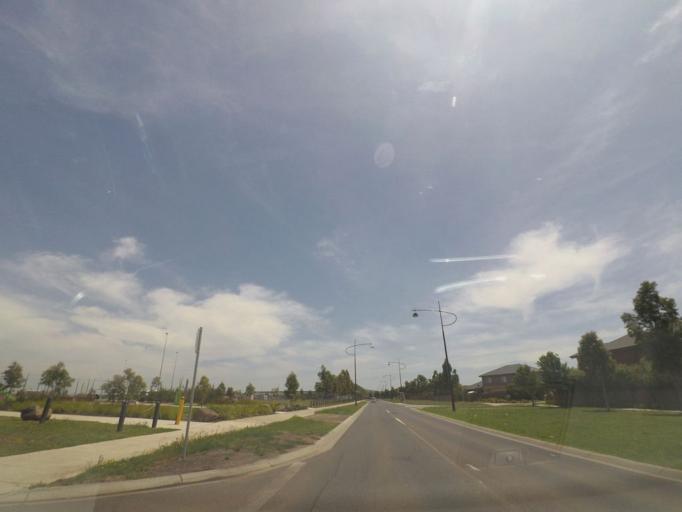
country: AU
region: Victoria
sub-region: Hume
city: Roxburgh Park
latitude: -37.6197
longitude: 144.9187
